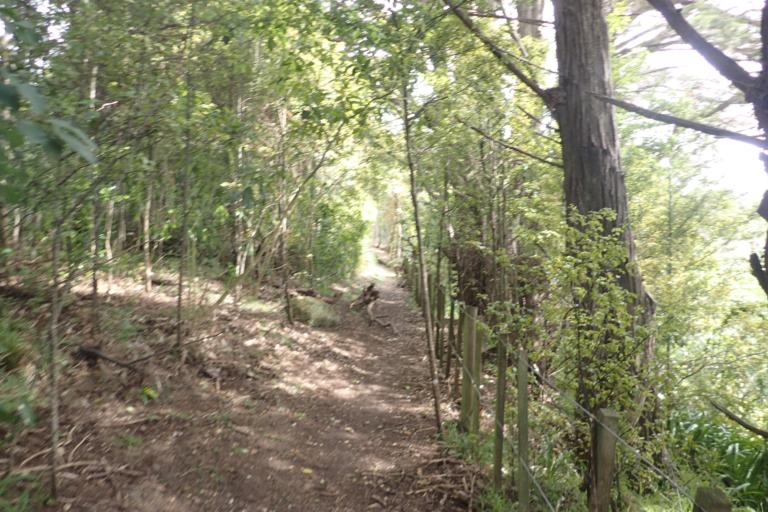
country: NZ
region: Auckland
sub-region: Auckland
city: Pakuranga
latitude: -36.7875
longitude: 175.0065
